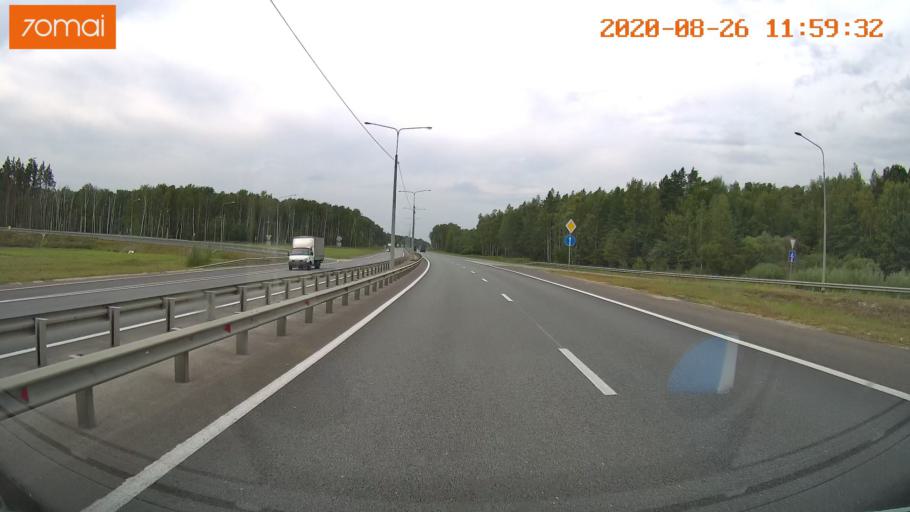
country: RU
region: Rjazan
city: Kiritsy
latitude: 54.2862
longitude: 40.2973
